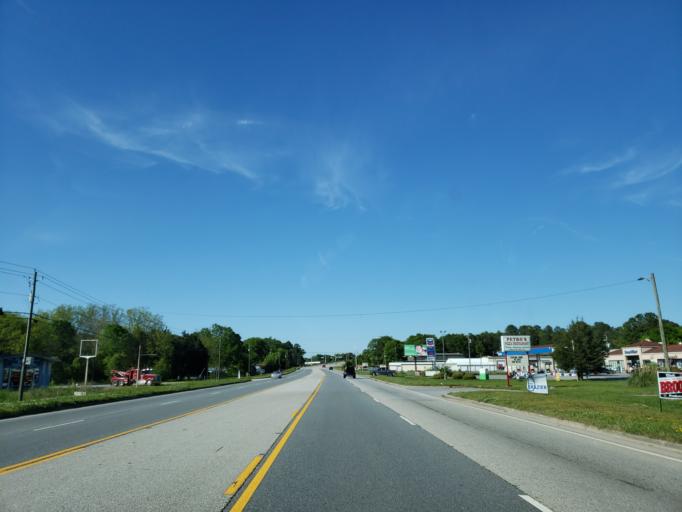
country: US
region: Georgia
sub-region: Polk County
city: Cedartown
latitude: 33.9834
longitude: -85.2558
